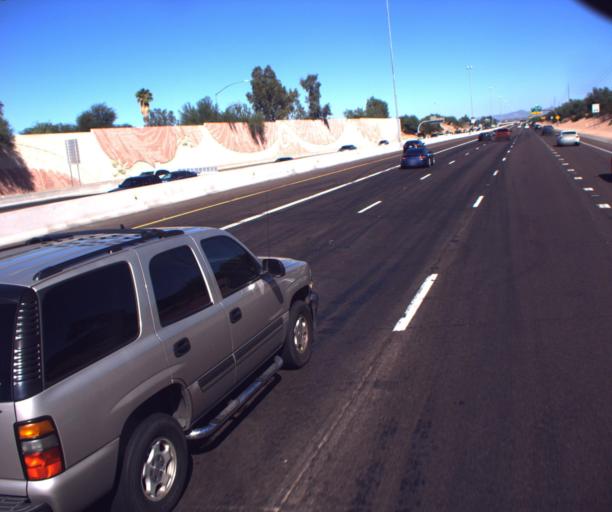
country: US
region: Arizona
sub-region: Maricopa County
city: Paradise Valley
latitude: 33.5864
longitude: -111.8914
